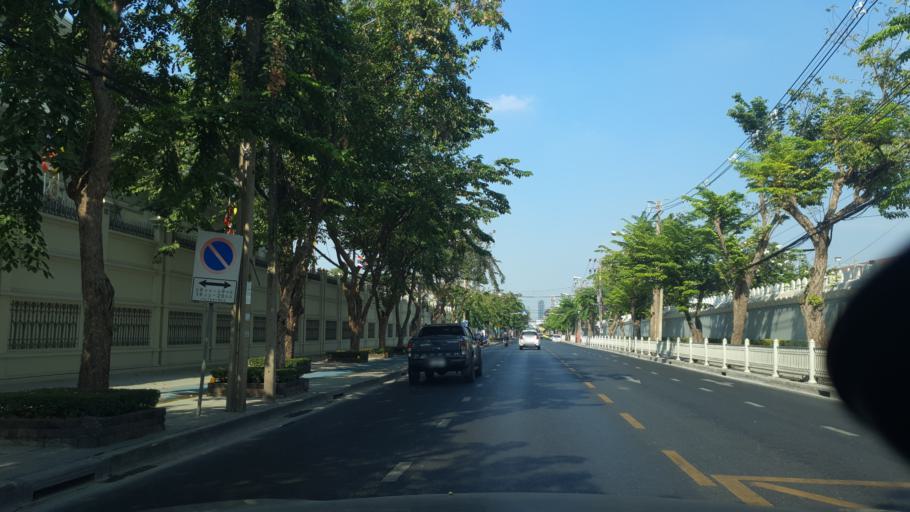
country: TH
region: Bangkok
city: Dusit
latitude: 13.7759
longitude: 100.5139
